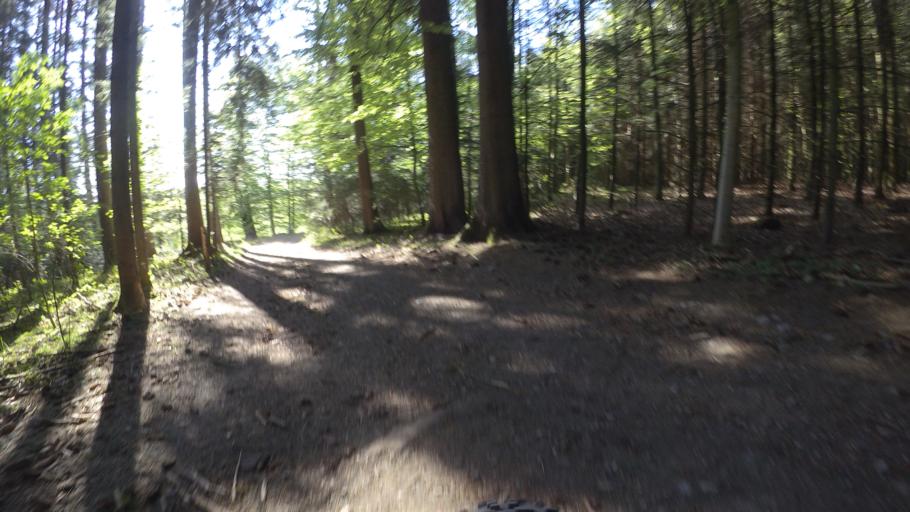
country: DE
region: Bavaria
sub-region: Upper Bavaria
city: Traunreut
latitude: 47.9365
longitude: 12.5672
